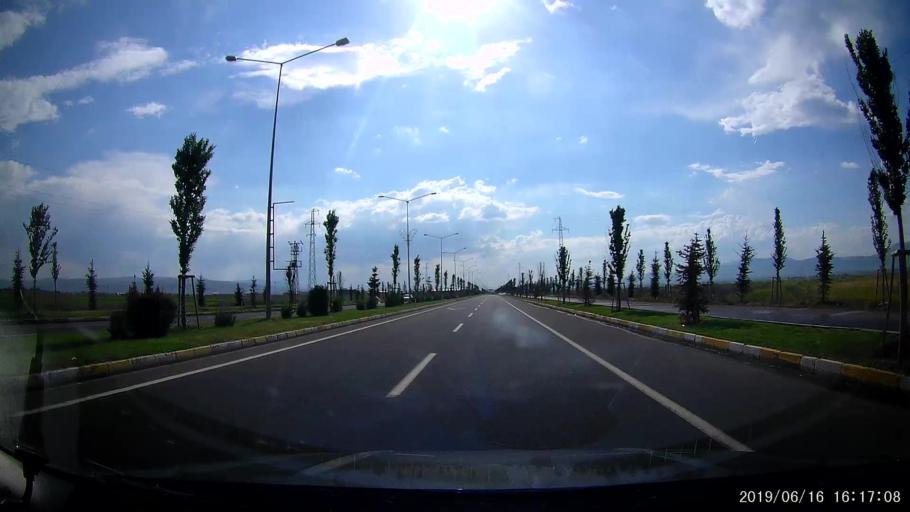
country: TR
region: Erzurum
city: Ilica
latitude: 39.9636
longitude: 41.1935
